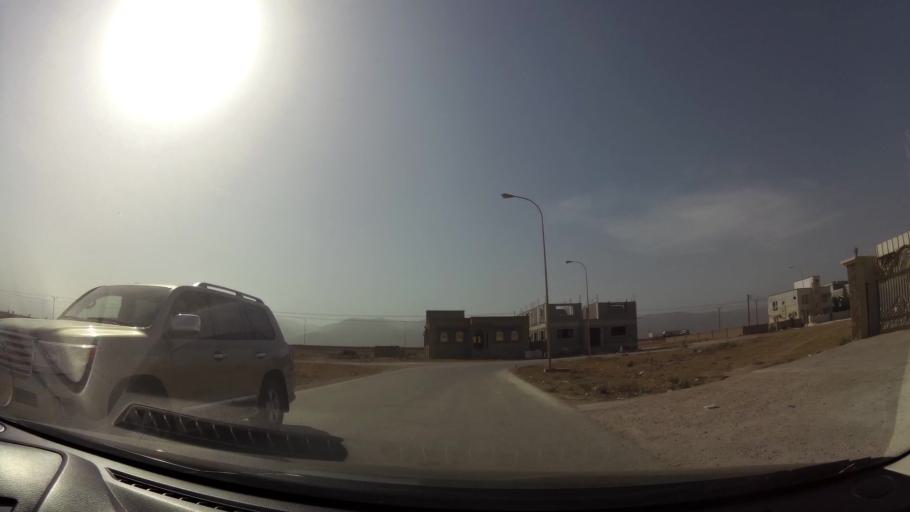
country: OM
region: Zufar
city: Salalah
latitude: 17.0143
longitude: 54.0074
